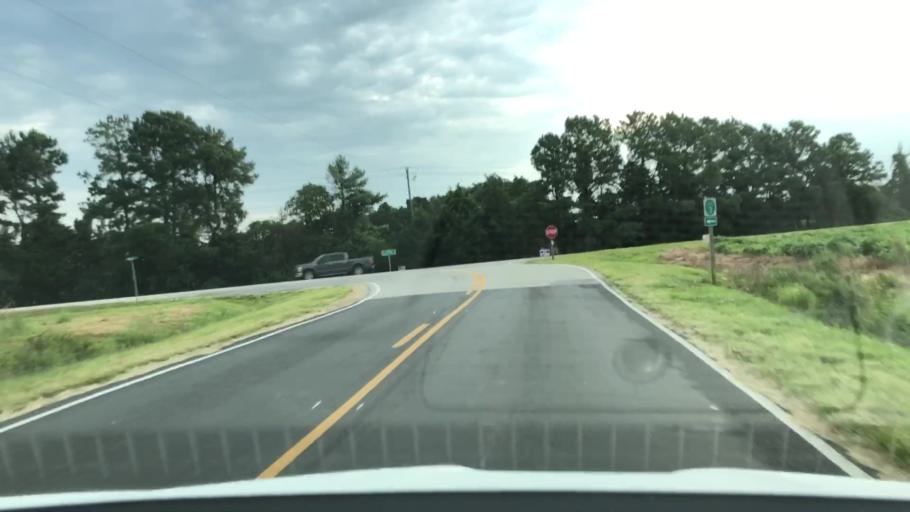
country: US
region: North Carolina
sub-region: Jones County
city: Trenton
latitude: 35.0007
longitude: -77.2740
